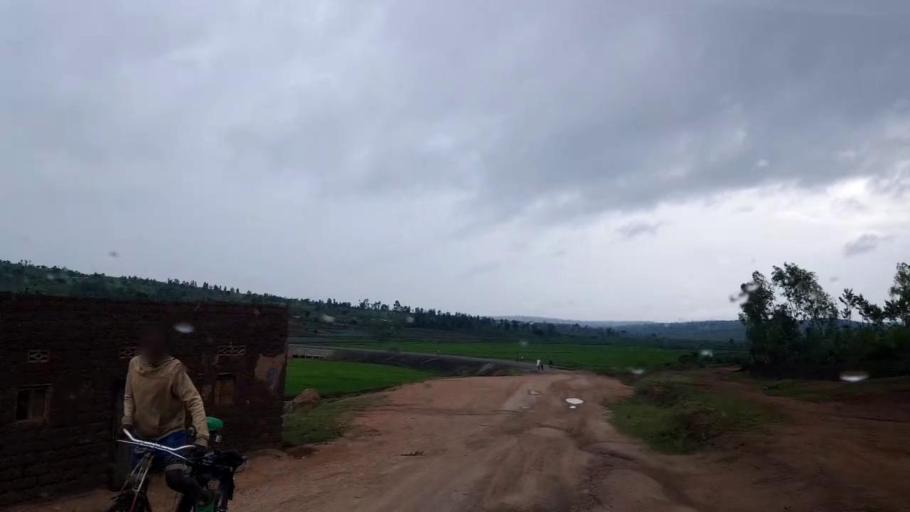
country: RW
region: Northern Province
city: Byumba
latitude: -1.4262
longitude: 30.2726
